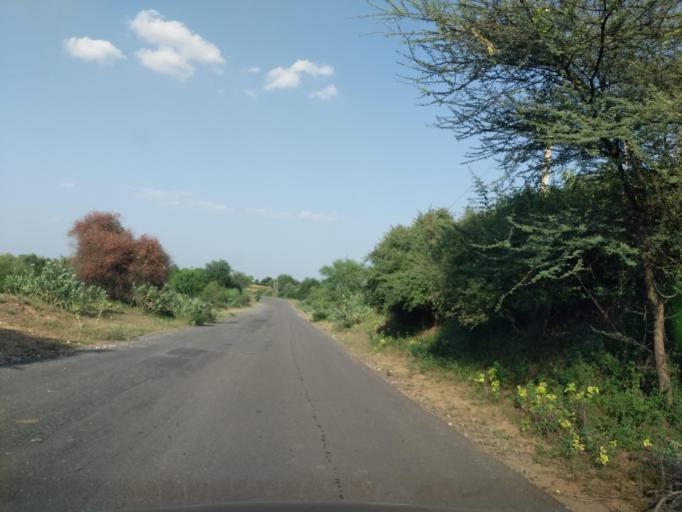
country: IN
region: Rajasthan
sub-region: Churu
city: Rajgarh
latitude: 28.4976
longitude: 75.3784
